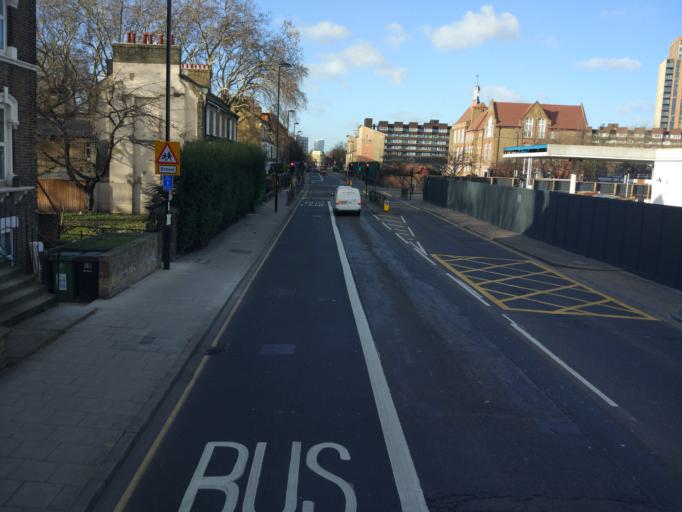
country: GB
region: England
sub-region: Greater London
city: Poplar
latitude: 51.4872
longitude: -0.0372
